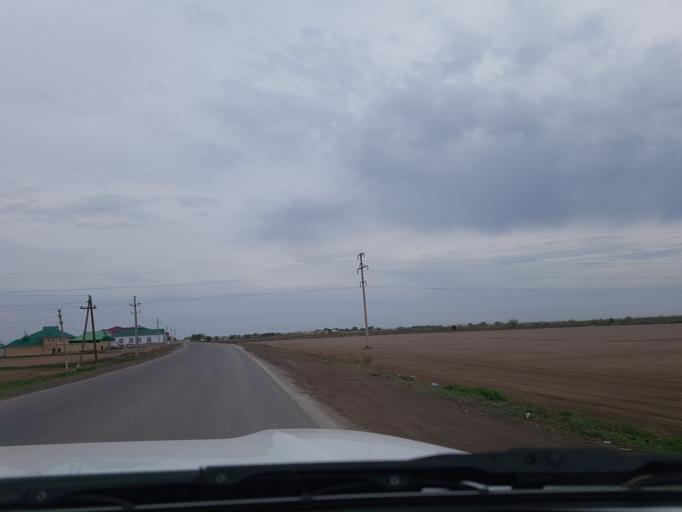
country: TM
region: Lebap
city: Turkmenabat
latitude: 39.0660
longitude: 63.5586
